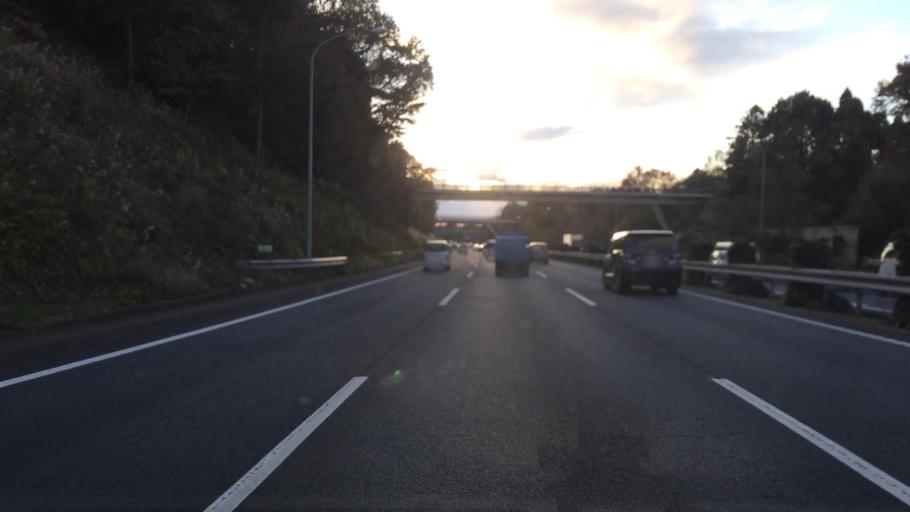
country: JP
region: Chiba
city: Shisui
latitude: 35.6985
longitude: 140.2599
